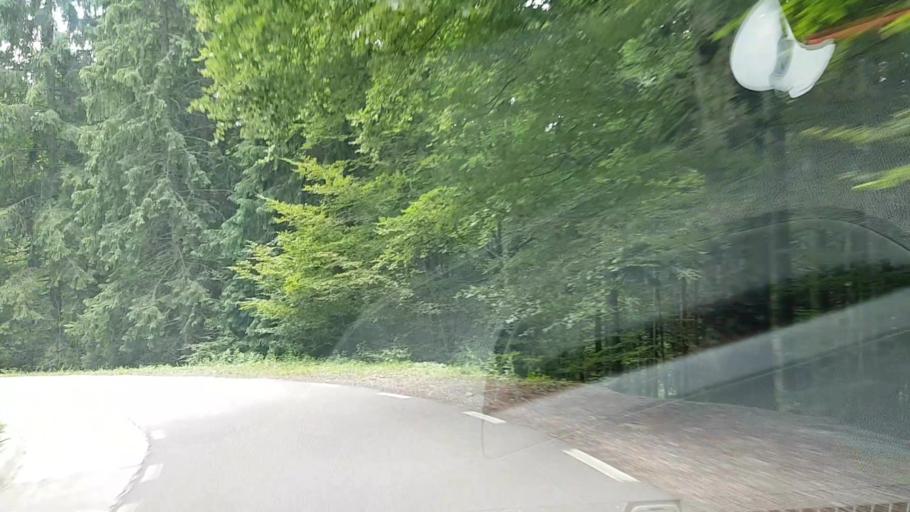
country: RO
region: Suceava
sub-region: Comuna Crucea
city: Crucea
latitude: 47.4308
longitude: 25.5718
